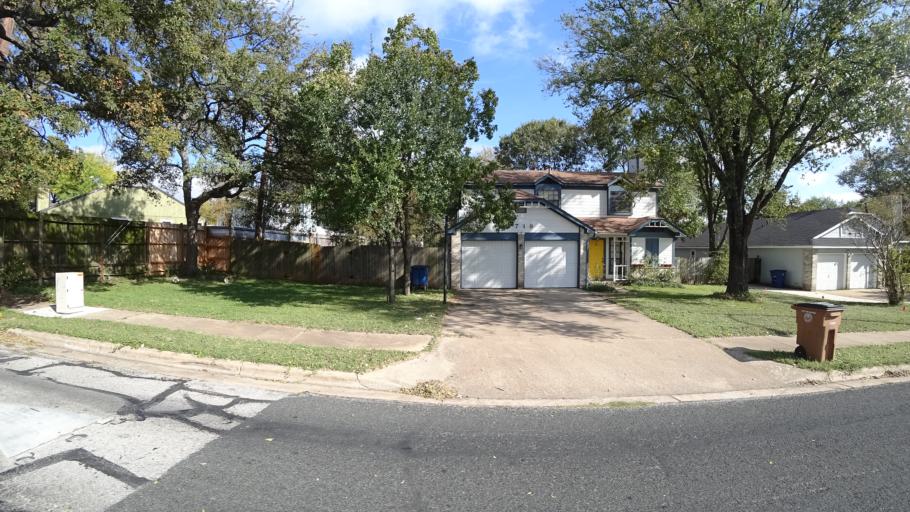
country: US
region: Texas
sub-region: Travis County
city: Shady Hollow
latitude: 30.1929
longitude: -97.8272
